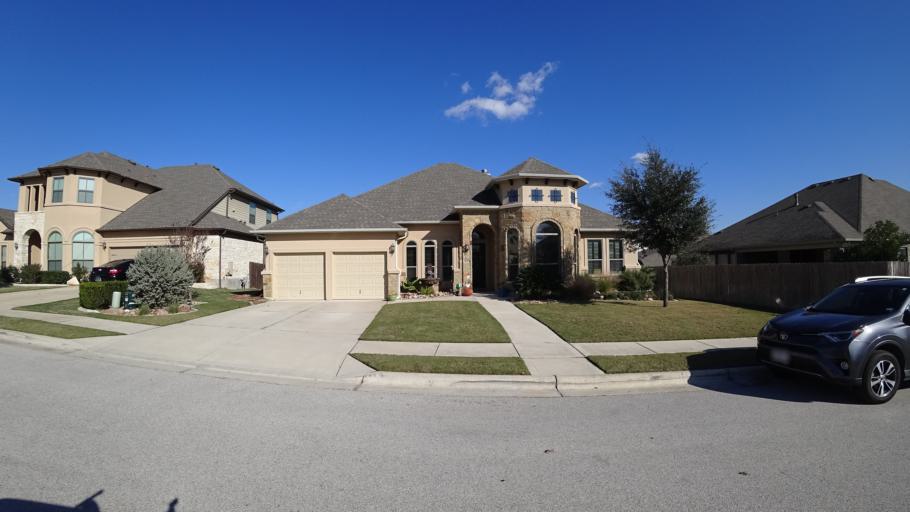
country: US
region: Texas
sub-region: Williamson County
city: Brushy Creek
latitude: 30.4864
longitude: -97.7249
